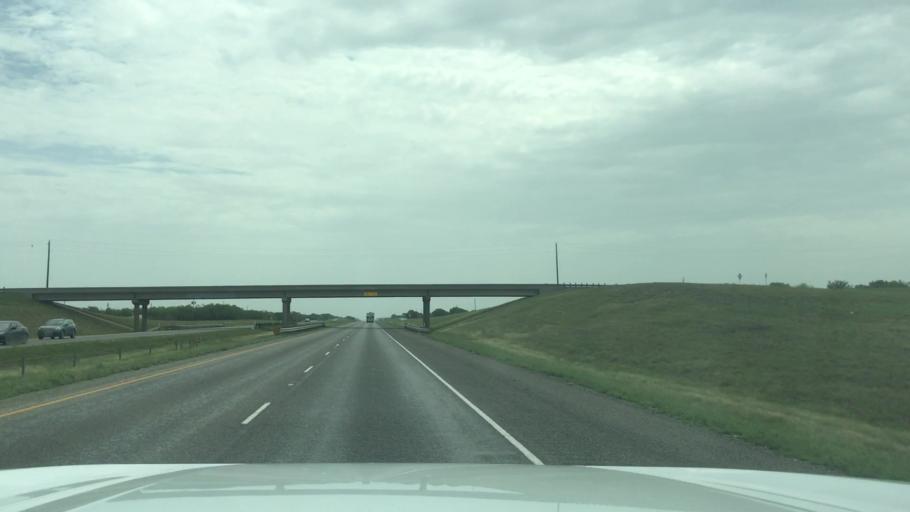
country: US
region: Texas
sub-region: Eastland County
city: Cisco
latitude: 32.3754
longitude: -98.9238
